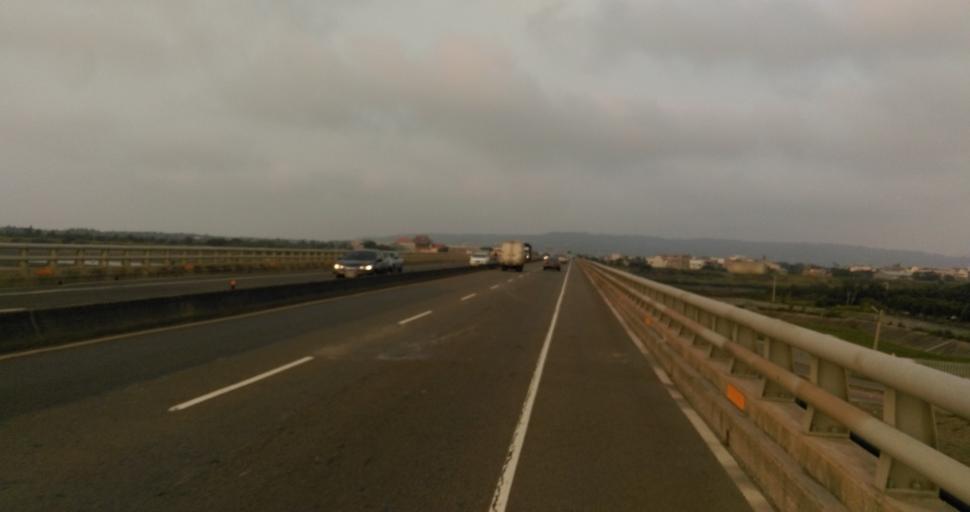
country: TW
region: Taiwan
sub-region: Hsinchu
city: Hsinchu
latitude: 24.8470
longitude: 120.9384
